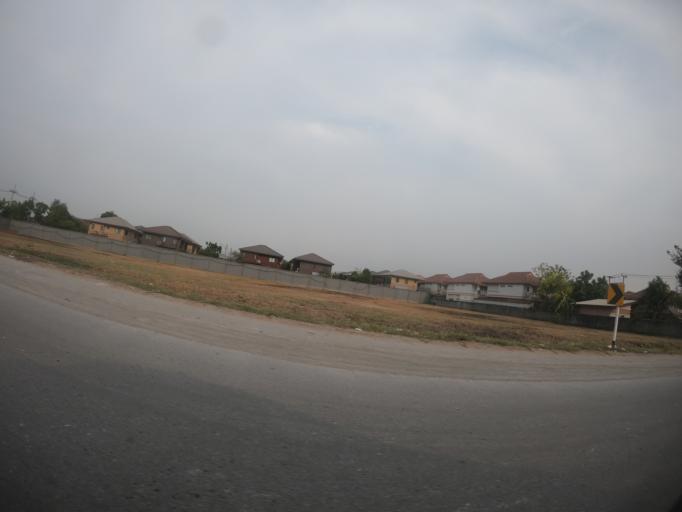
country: TH
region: Phra Nakhon Si Ayutthaya
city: Ban Bang Kadi Pathum Thani
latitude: 14.0037
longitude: 100.5715
